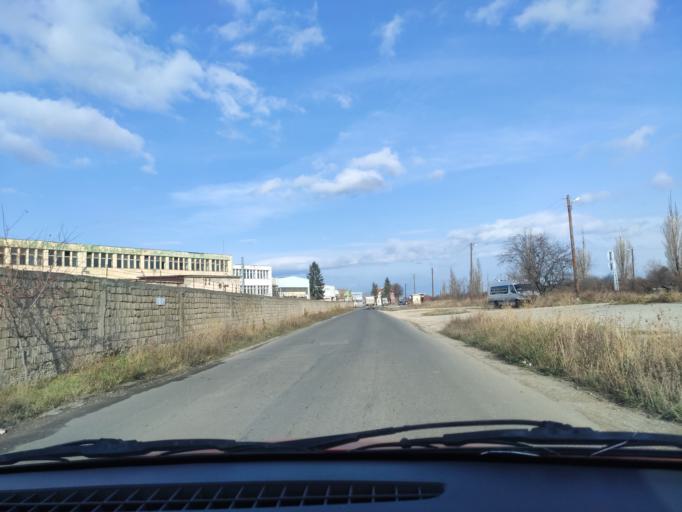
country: RO
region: Brasov
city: Codlea
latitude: 45.6904
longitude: 25.4567
